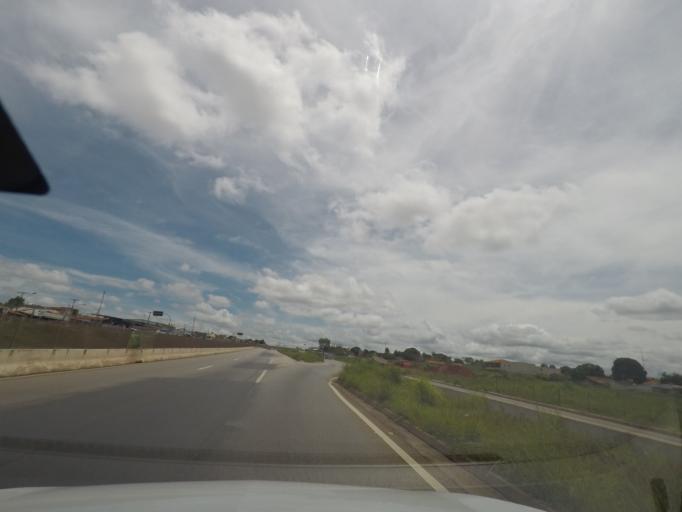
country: BR
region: Goias
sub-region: Goiania
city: Goiania
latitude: -16.7190
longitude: -49.3690
